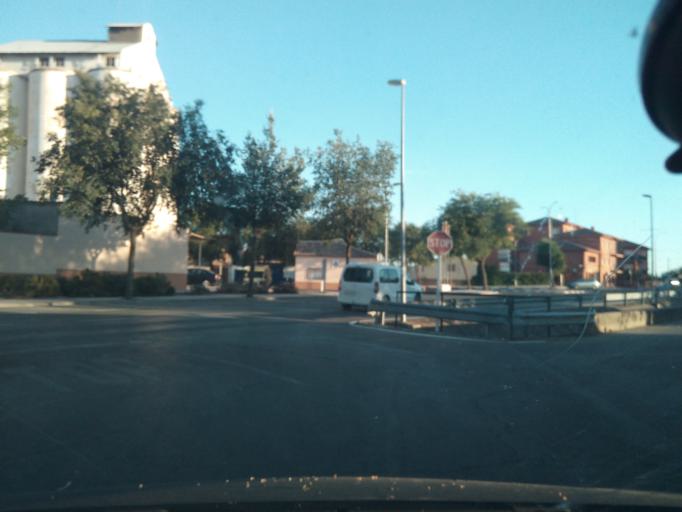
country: ES
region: Castille-La Mancha
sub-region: Province of Toledo
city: Villacanas
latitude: 39.6164
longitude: -3.3396
